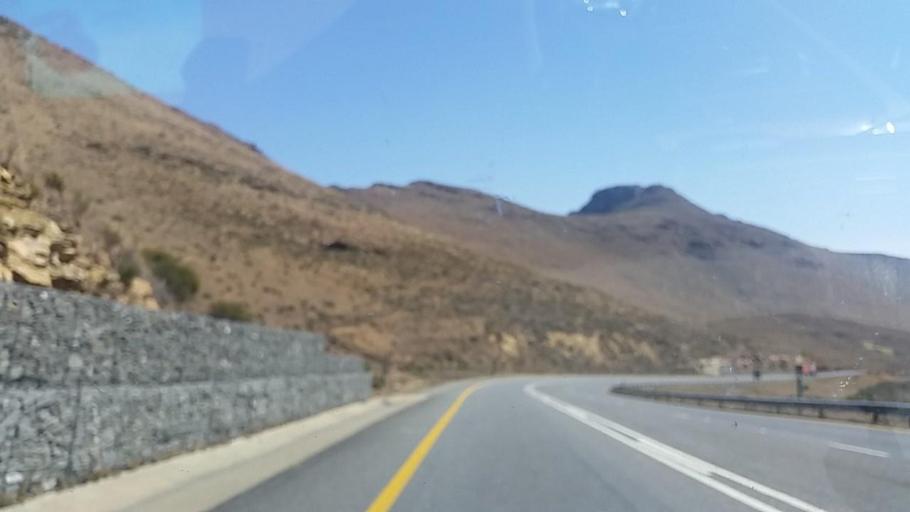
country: ZA
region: Eastern Cape
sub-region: Chris Hani District Municipality
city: Middelburg
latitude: -31.8324
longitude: 24.8569
